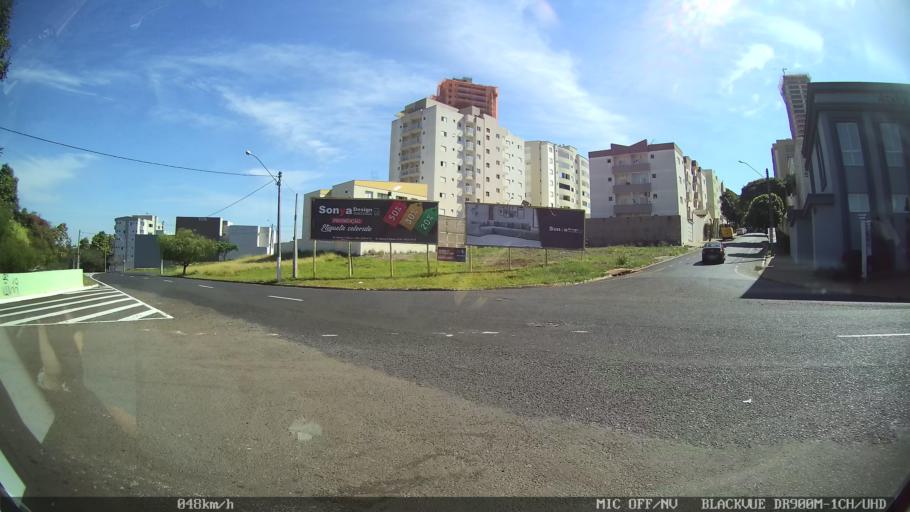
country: BR
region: Sao Paulo
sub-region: Franca
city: Franca
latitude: -20.5547
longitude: -47.4143
